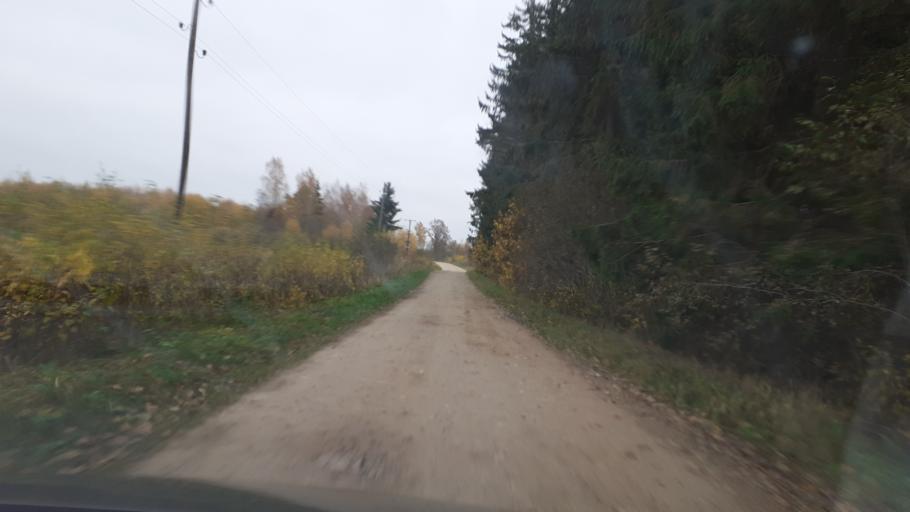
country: LV
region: Saldus Rajons
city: Saldus
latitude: 56.8619
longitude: 22.3314
